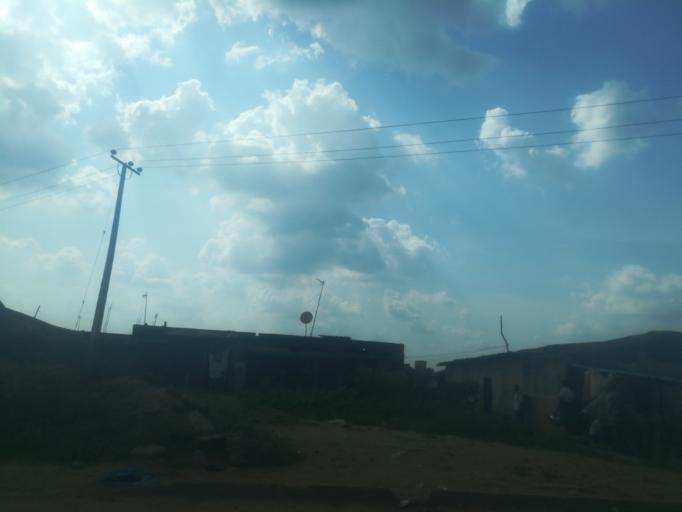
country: NG
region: Ogun
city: Abeokuta
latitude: 7.1780
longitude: 3.3405
